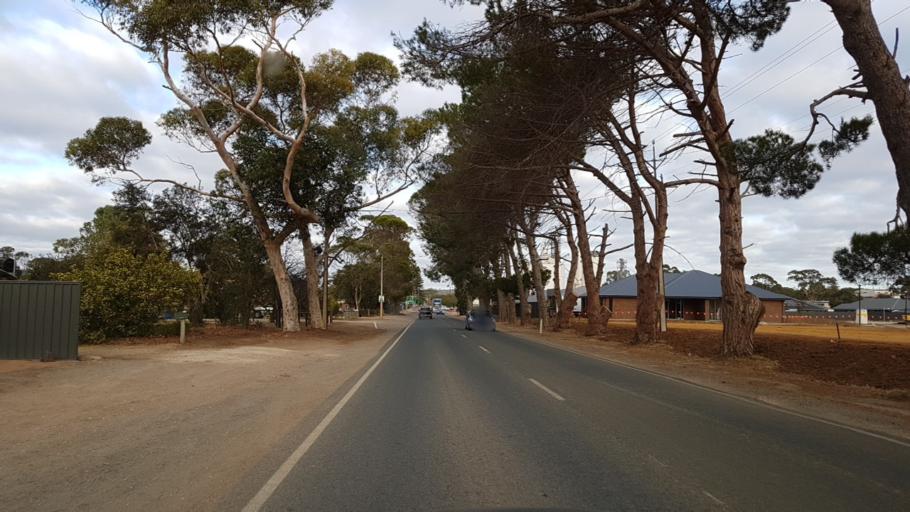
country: AU
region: South Australia
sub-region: Alexandrina
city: Strathalbyn
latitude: -35.2562
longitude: 138.9035
